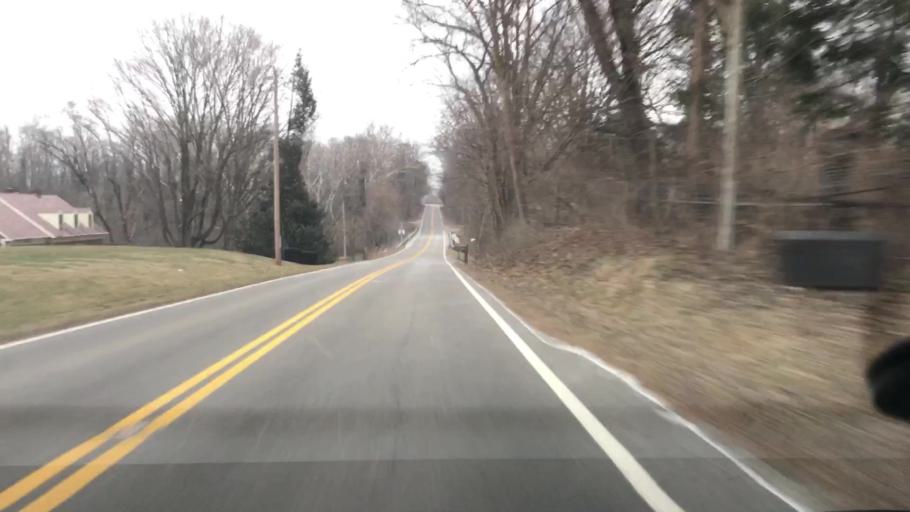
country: US
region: Ohio
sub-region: Clark County
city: Springfield
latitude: 39.8805
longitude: -83.8467
